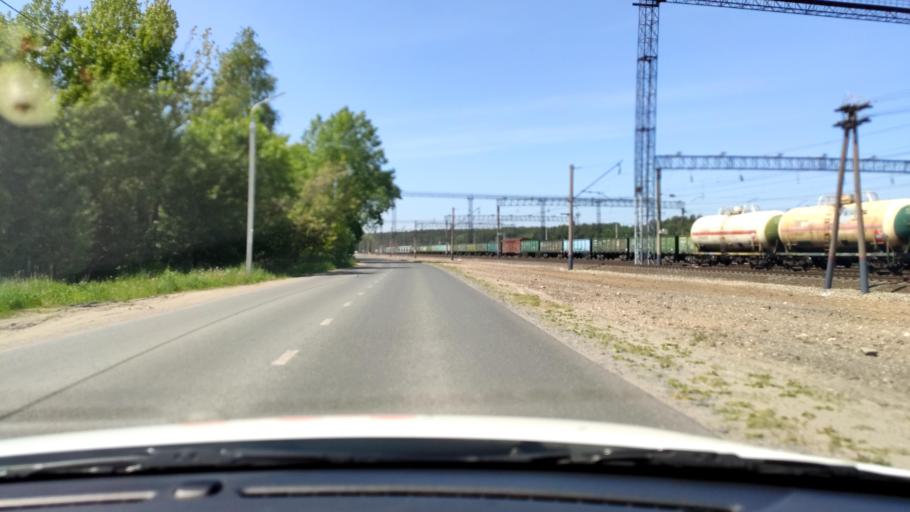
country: RU
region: Tatarstan
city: Osinovo
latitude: 55.8201
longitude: 48.8584
